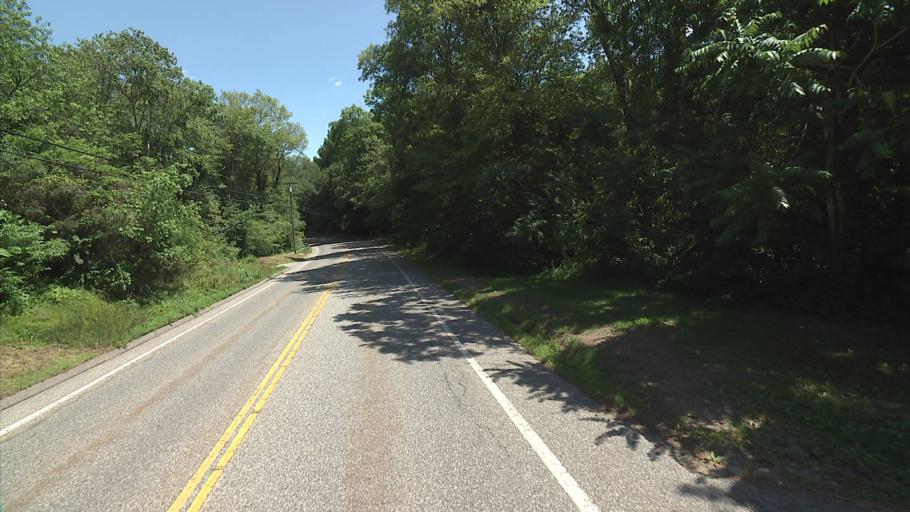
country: US
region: Connecticut
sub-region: New London County
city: Preston City
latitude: 41.4840
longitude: -71.9021
